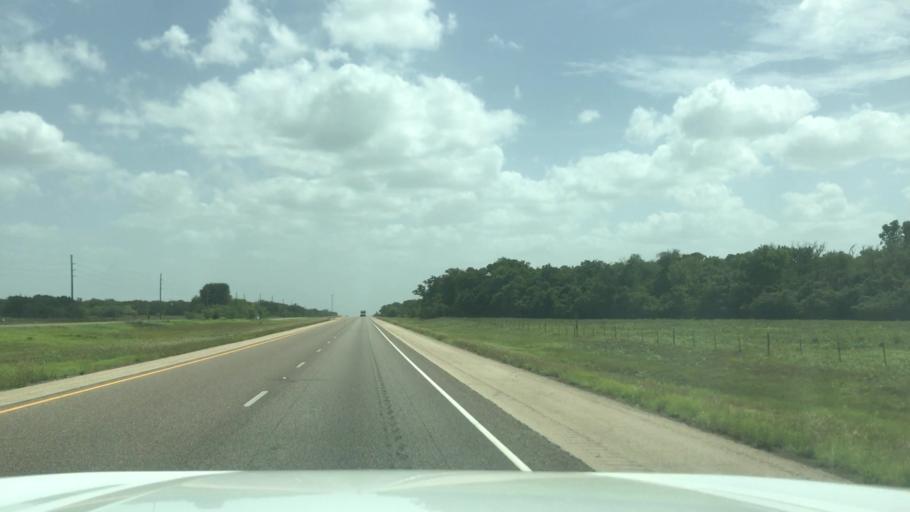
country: US
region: Texas
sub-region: Robertson County
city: Calvert
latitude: 31.0515
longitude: -96.7113
